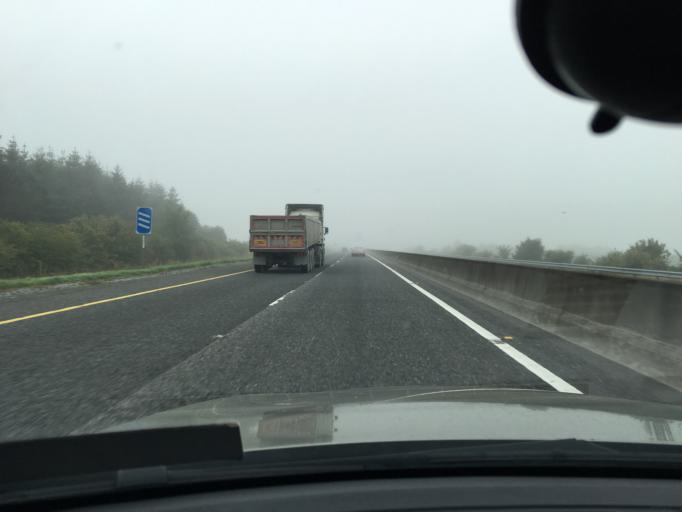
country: IE
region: Leinster
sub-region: An Iarmhi
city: Rochfortbridge
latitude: 53.4105
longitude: -7.2725
